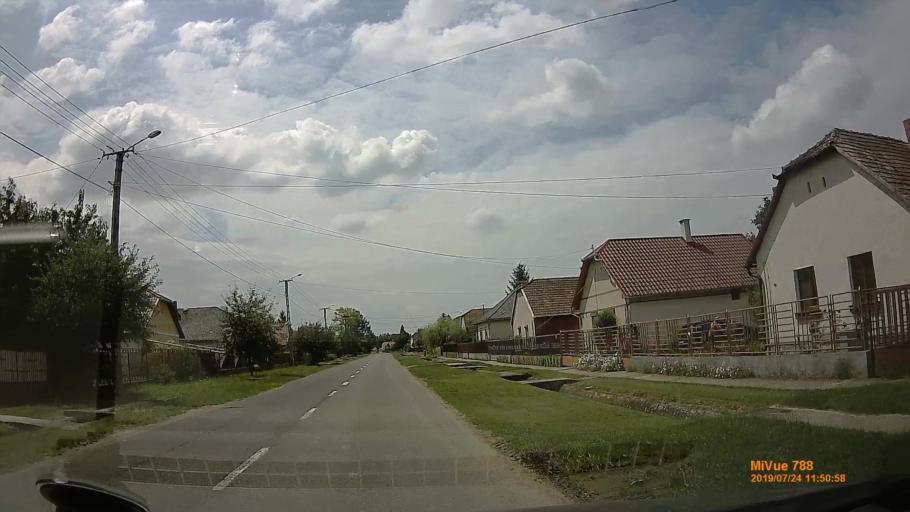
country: UA
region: Zakarpattia
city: Batiovo
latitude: 48.2371
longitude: 22.4349
